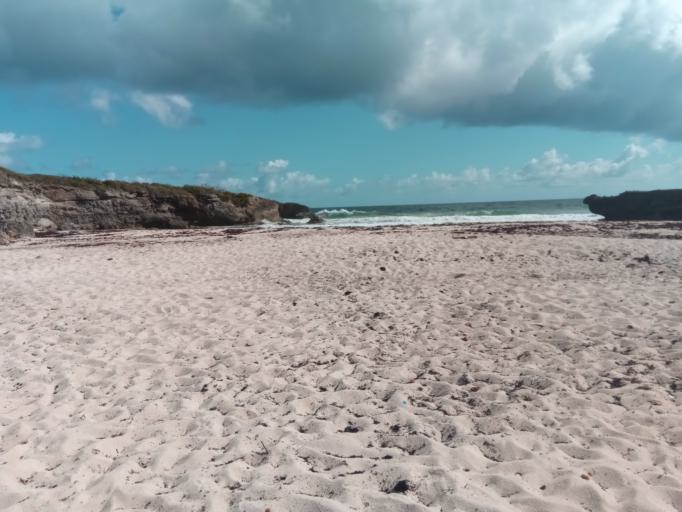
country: GP
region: Guadeloupe
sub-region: Guadeloupe
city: Saint-Francois
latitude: 16.2732
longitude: -61.2434
